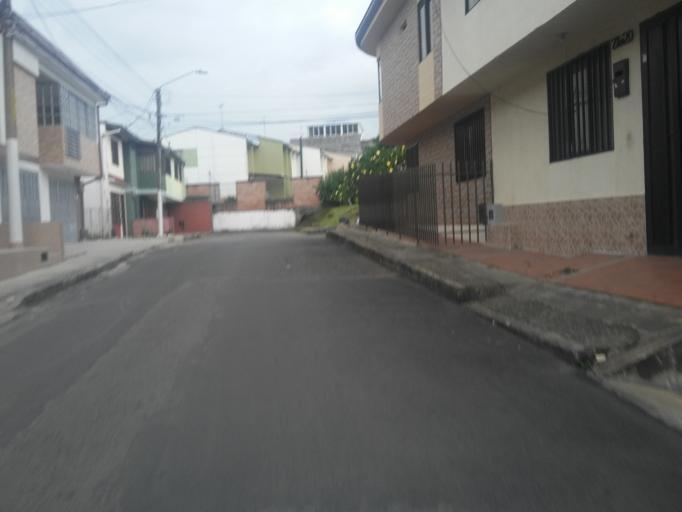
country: CO
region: Cauca
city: Popayan
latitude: 2.4611
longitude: -76.5885
